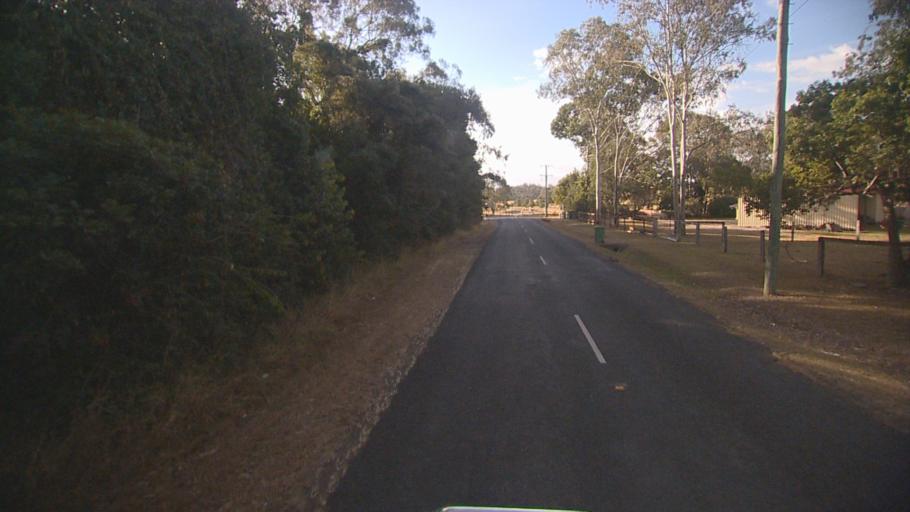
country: AU
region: Queensland
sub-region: Logan
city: Cedar Vale
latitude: -27.8679
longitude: 153.0114
